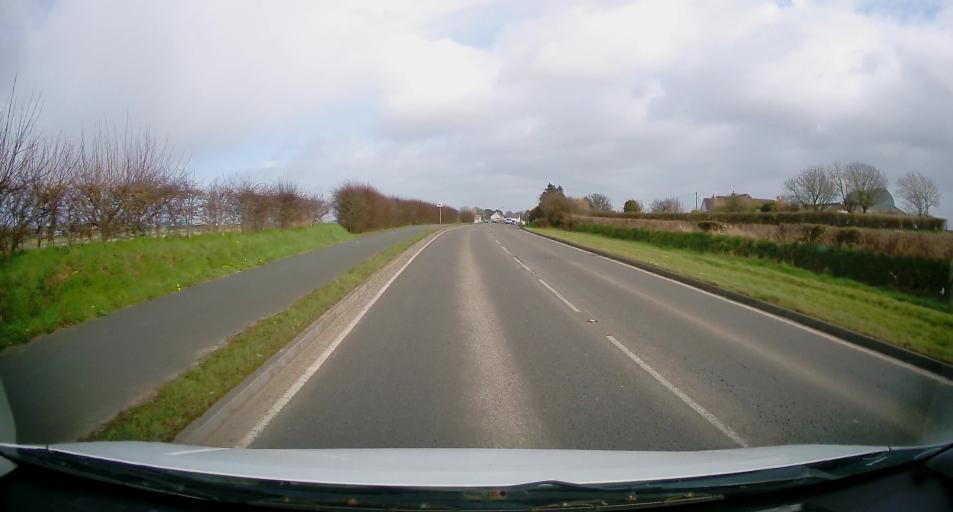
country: GB
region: Wales
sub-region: County of Ceredigion
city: Aberporth
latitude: 52.1118
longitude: -4.5678
